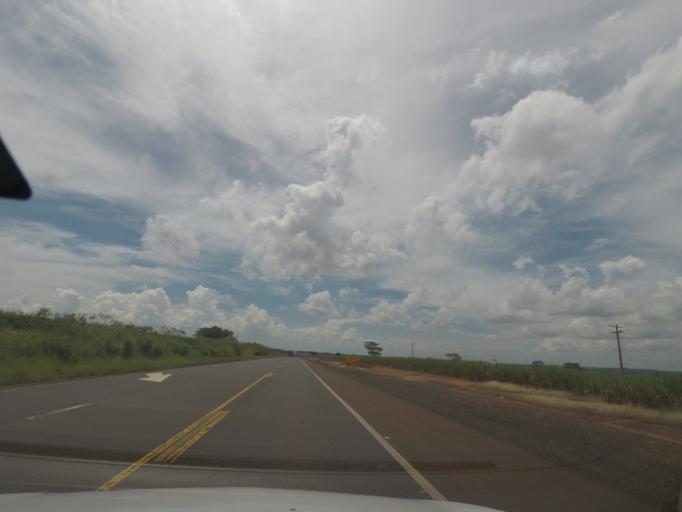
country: BR
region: Sao Paulo
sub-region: Barretos
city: Barretos
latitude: -20.3838
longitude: -48.6417
